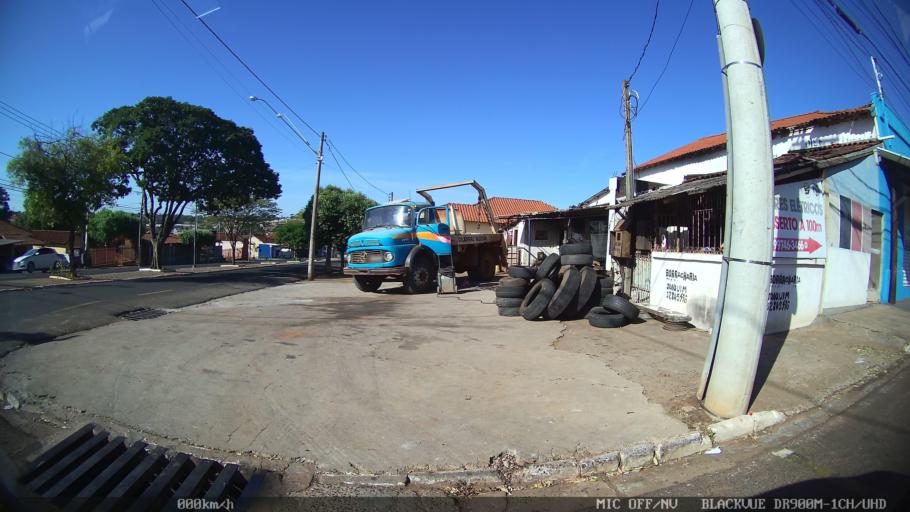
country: BR
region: Sao Paulo
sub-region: Olimpia
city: Olimpia
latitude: -20.7450
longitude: -48.9096
